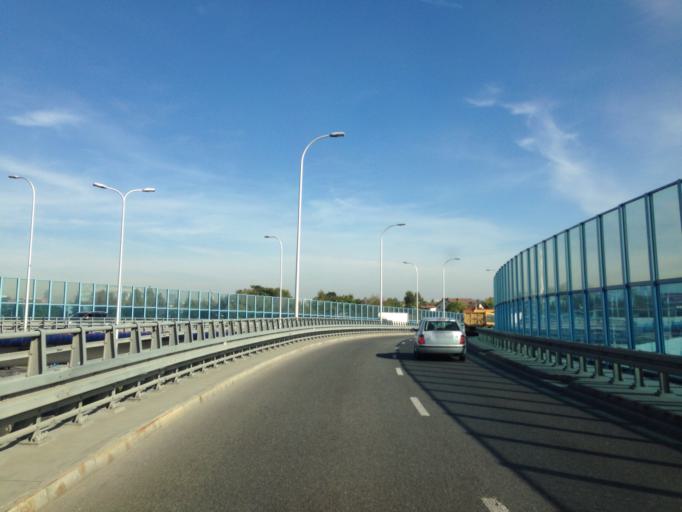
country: PL
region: Masovian Voivodeship
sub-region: Warszawa
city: Wlochy
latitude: 52.1954
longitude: 20.9282
